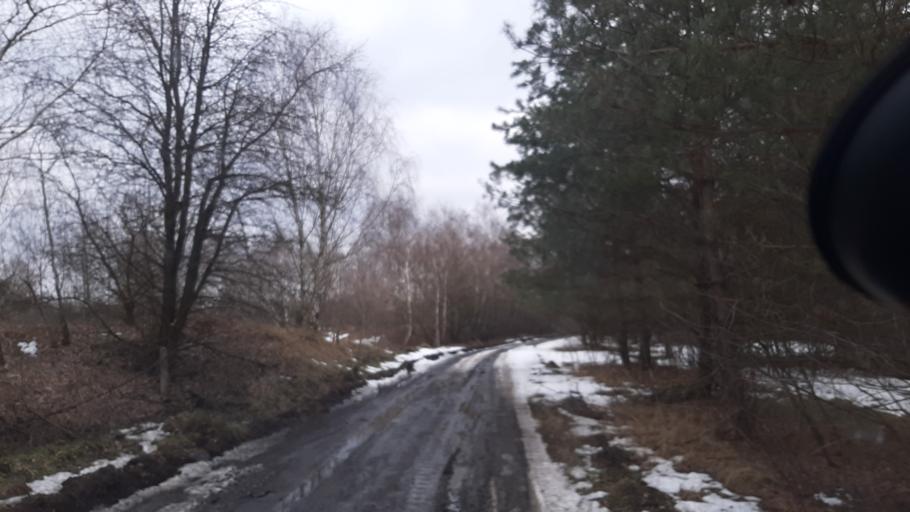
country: PL
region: Lublin Voivodeship
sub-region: Powiat wlodawski
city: Wlodawa
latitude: 51.5157
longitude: 23.6041
